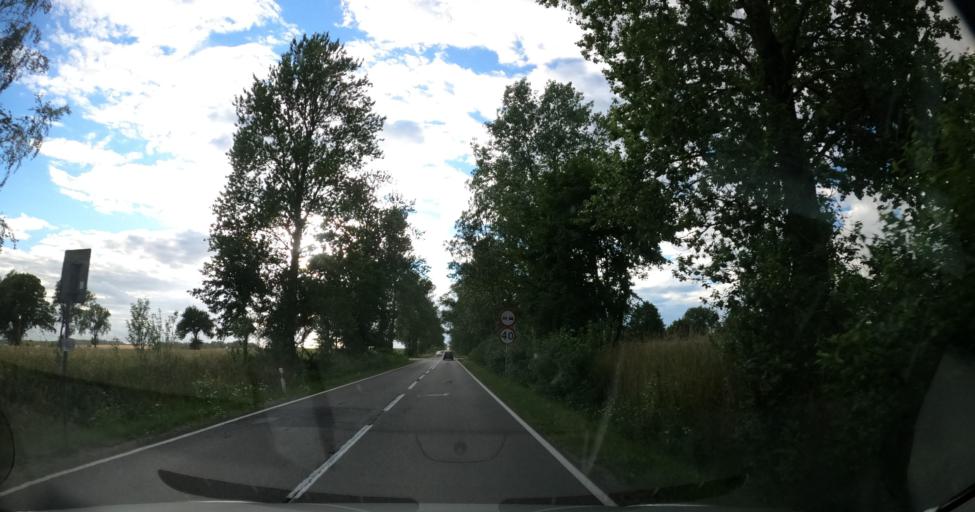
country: PL
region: Pomeranian Voivodeship
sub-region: Powiat slupski
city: Damnica
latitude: 54.4379
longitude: 17.3456
